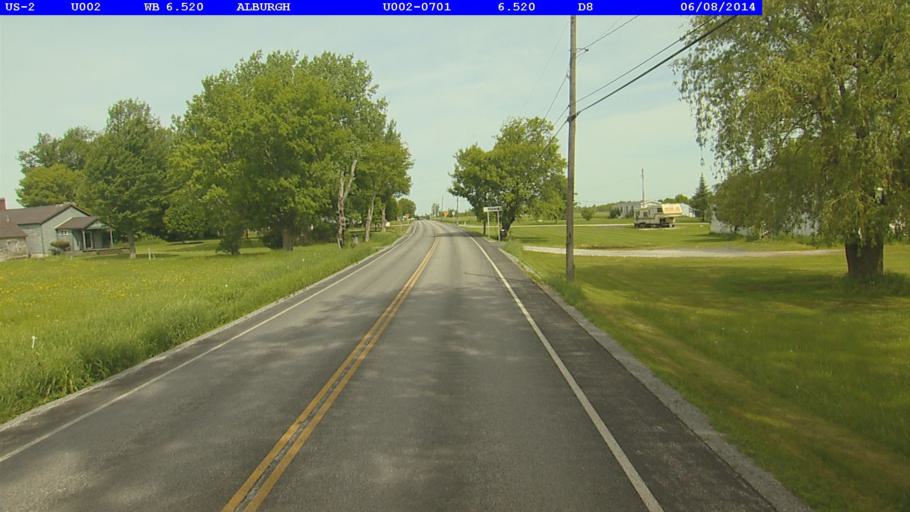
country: US
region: New York
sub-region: Clinton County
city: Rouses Point
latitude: 44.9565
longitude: -73.2734
